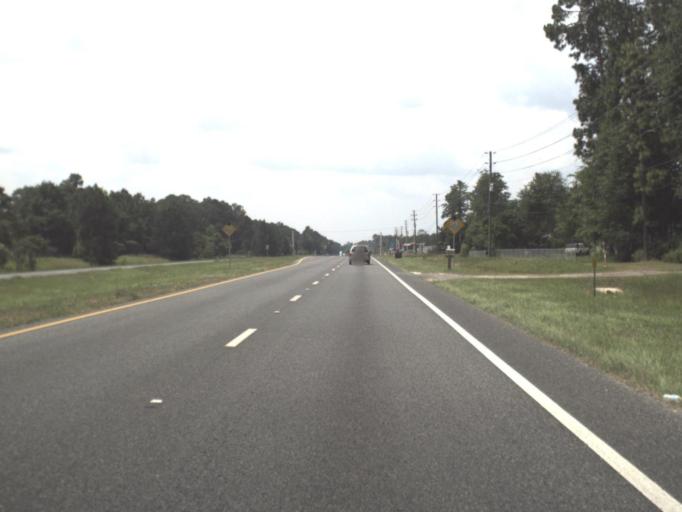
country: US
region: Florida
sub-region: Putnam County
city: Palatka
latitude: 29.7197
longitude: -81.6557
